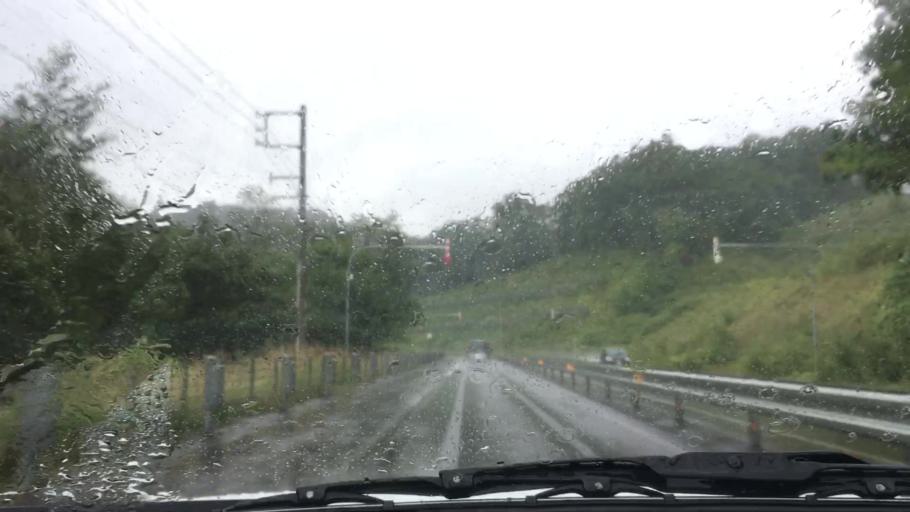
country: JP
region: Hokkaido
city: Otaru
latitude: 42.8494
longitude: 141.0444
